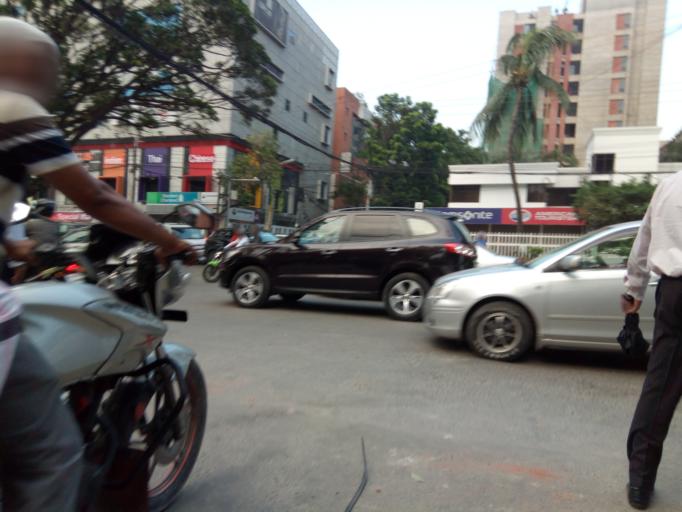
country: BD
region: Dhaka
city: Paltan
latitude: 23.7782
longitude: 90.4165
